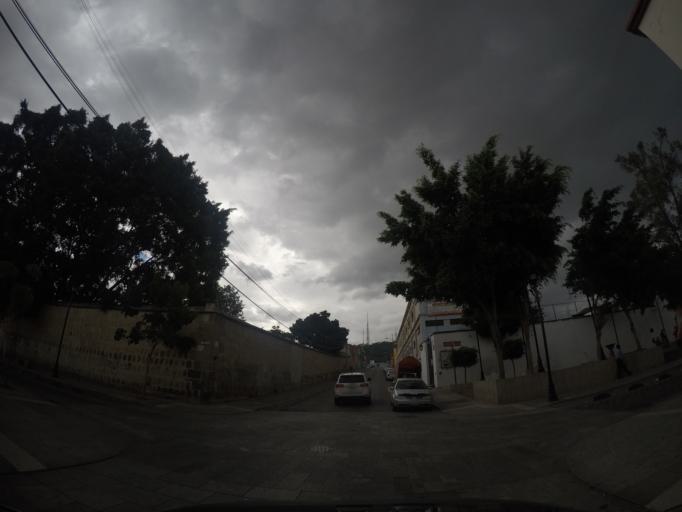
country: MX
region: Oaxaca
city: Oaxaca de Juarez
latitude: 17.0685
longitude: -96.7232
